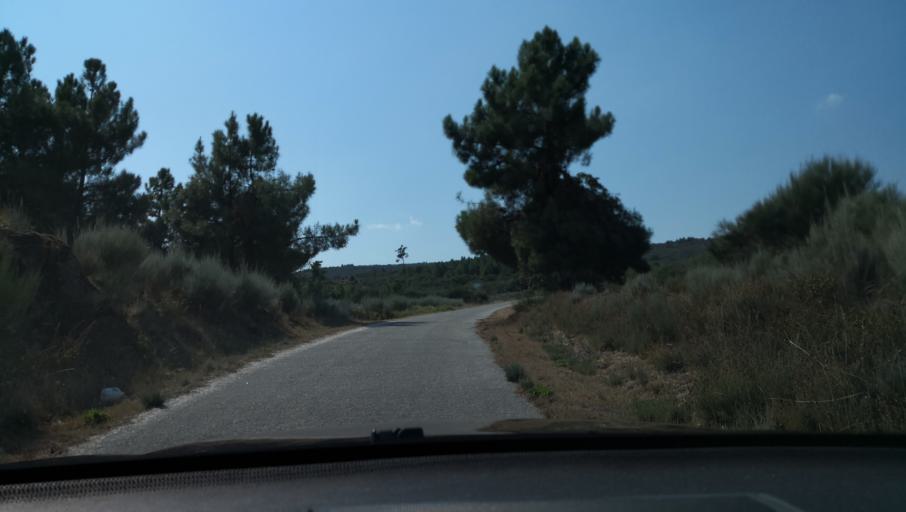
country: PT
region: Vila Real
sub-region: Sabrosa
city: Sabrosa
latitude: 41.3041
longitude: -7.5877
